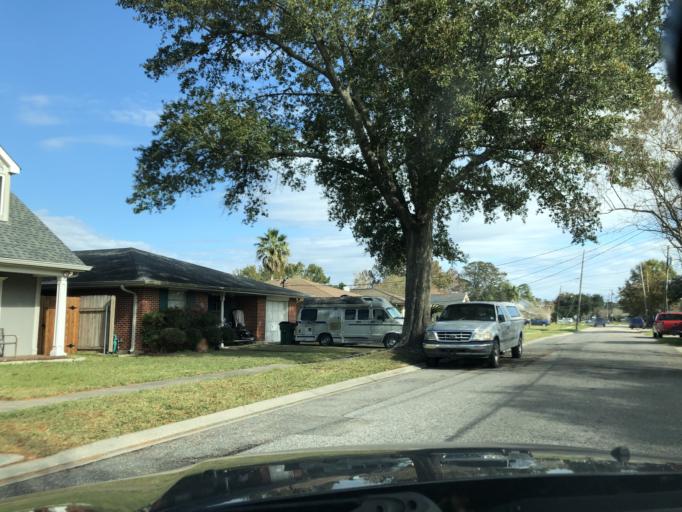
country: US
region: Louisiana
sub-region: Jefferson Parish
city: Metairie Terrace
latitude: 29.9855
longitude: -90.1660
